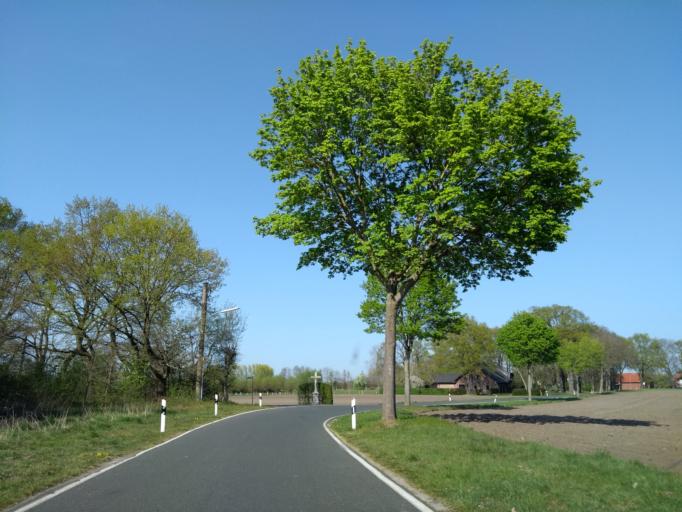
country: DE
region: North Rhine-Westphalia
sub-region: Regierungsbezirk Detmold
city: Delbruck
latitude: 51.7053
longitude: 8.5399
